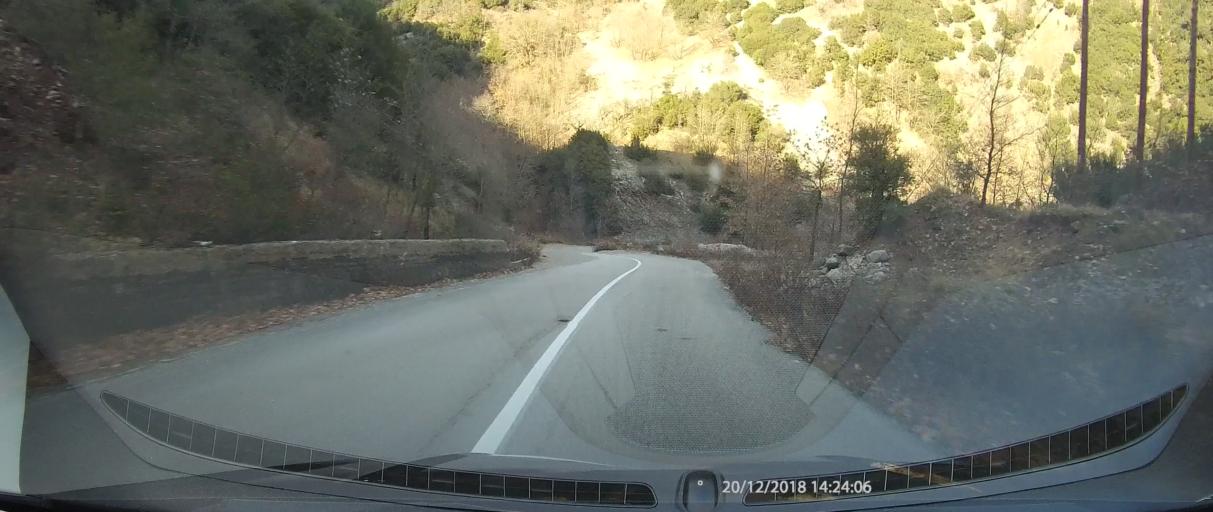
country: GR
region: West Greece
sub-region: Nomos Aitolias kai Akarnanias
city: Thermo
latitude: 38.7595
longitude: 21.6691
